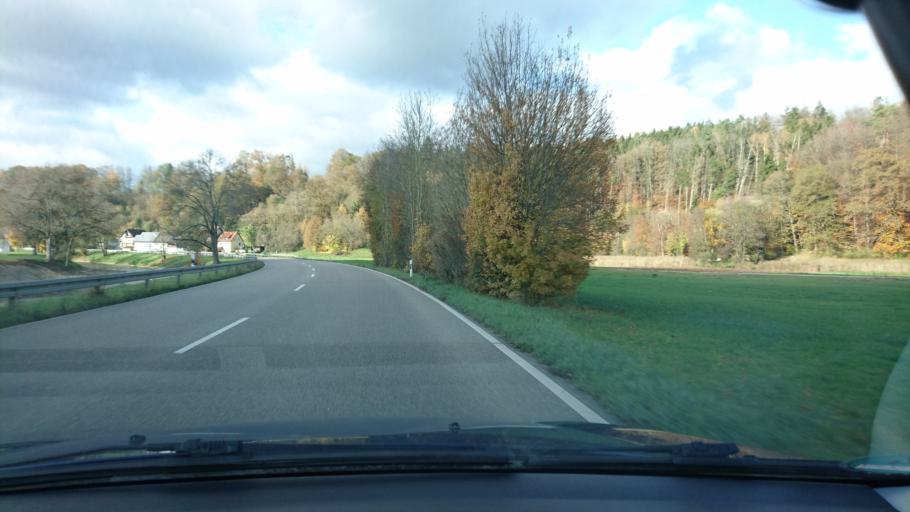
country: DE
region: Baden-Wuerttemberg
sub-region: Regierungsbezirk Stuttgart
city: Abtsgmund
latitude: 48.8973
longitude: 10.0059
